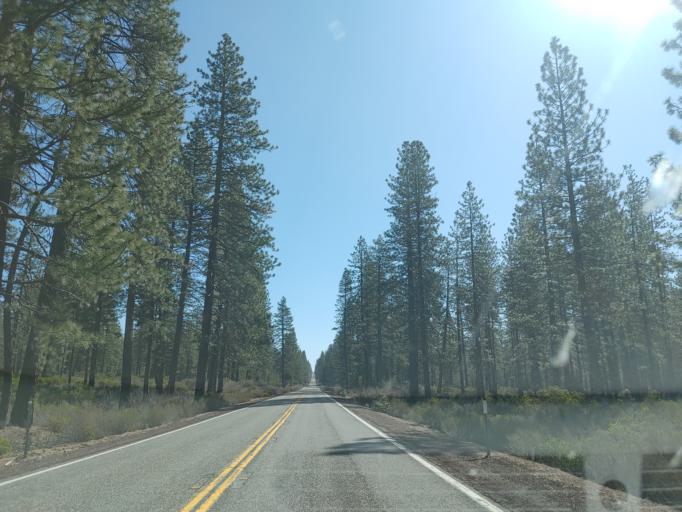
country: US
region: California
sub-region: Siskiyou County
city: McCloud
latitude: 41.2566
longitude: -122.0336
